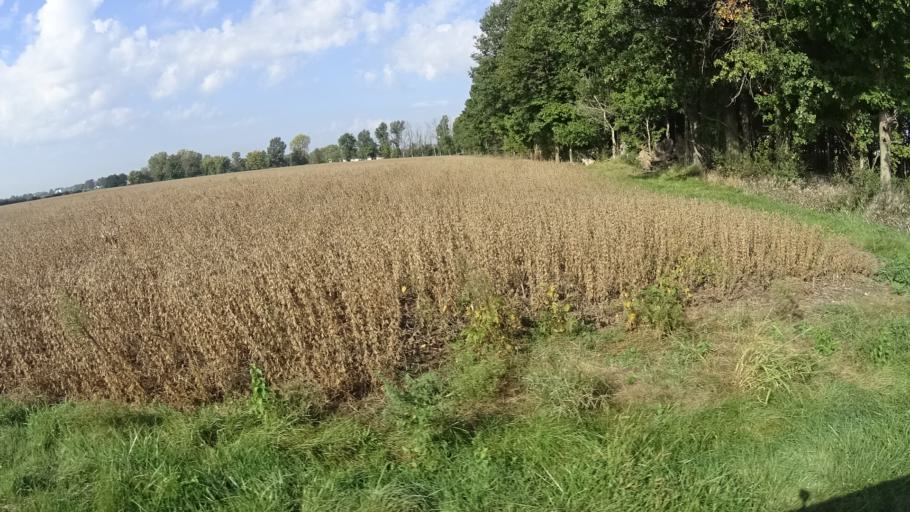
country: US
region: Indiana
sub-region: Madison County
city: Ingalls
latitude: 39.9951
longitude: -85.8243
